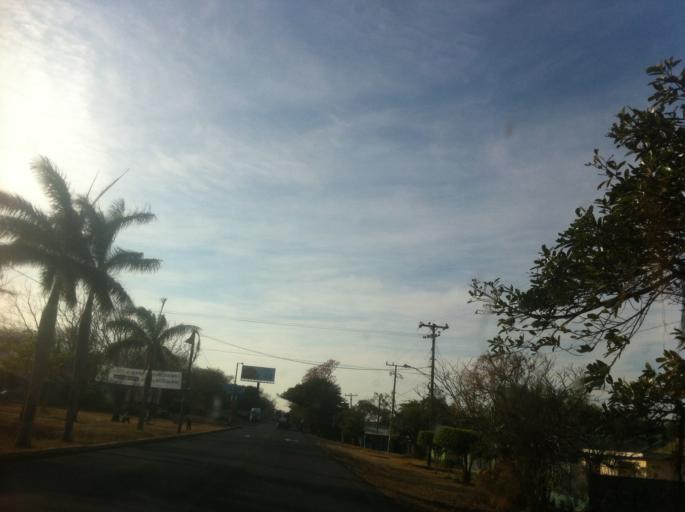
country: NI
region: Rivas
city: Rivas
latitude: 11.3535
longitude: -85.7409
